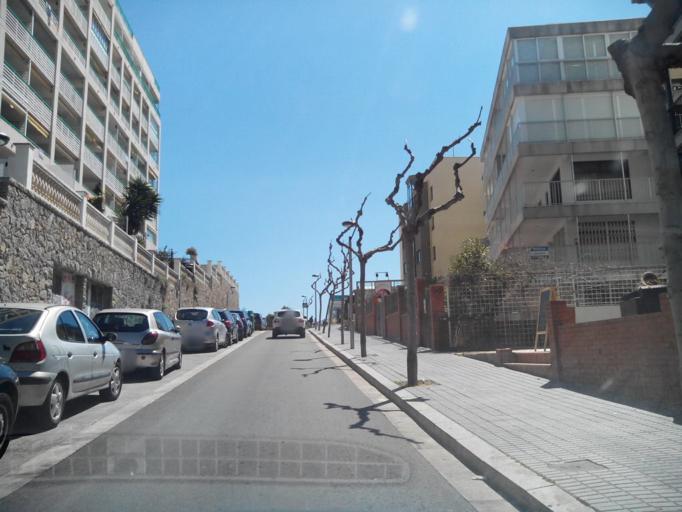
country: ES
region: Catalonia
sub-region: Provincia de Tarragona
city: Salou
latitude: 41.0708
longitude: 1.1458
